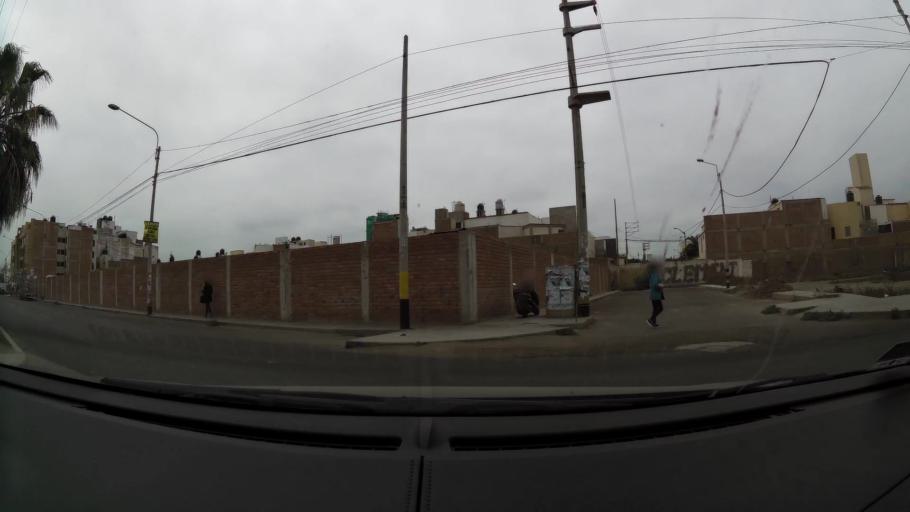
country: PE
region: La Libertad
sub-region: Provincia de Trujillo
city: Buenos Aires
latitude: -8.1364
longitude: -79.0352
